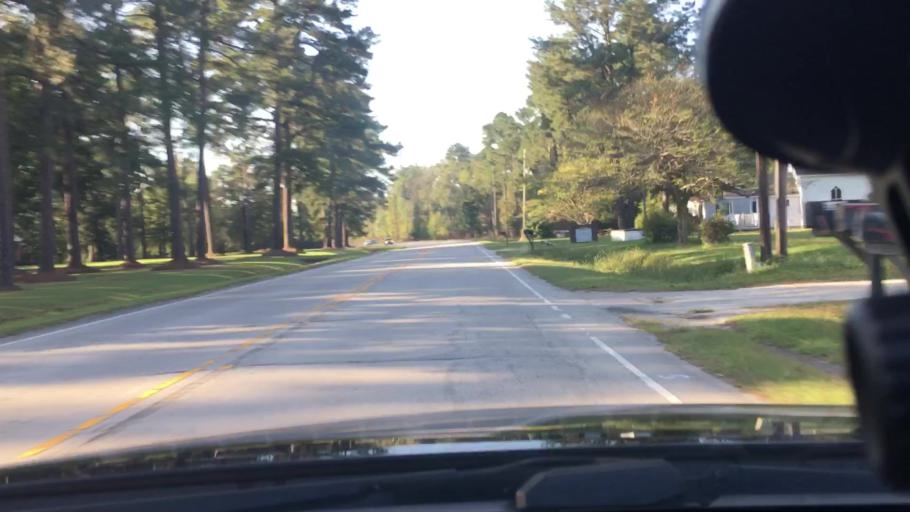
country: US
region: North Carolina
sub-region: Craven County
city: Vanceboro
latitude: 35.4081
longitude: -77.2440
